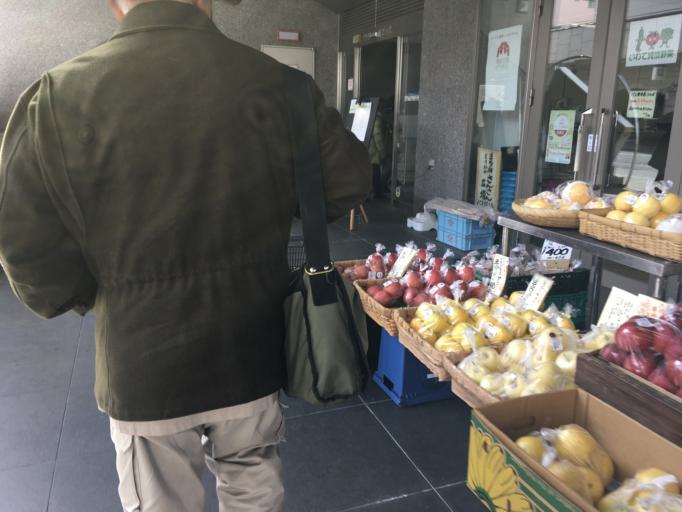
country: JP
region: Iwate
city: Morioka-shi
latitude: 39.7001
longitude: 141.1550
